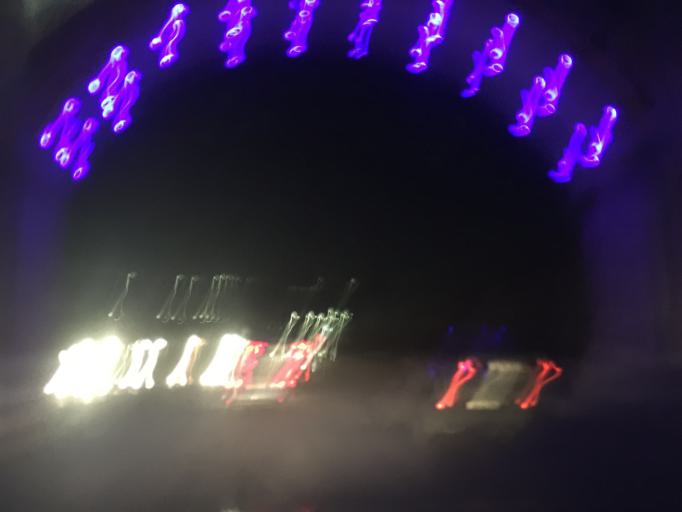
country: JO
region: Zarqa
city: Russeifa
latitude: 32.0188
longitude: 36.0031
